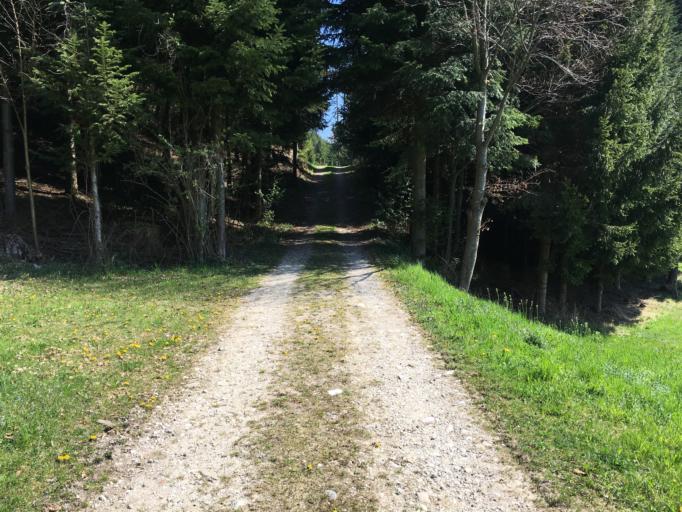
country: AT
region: Upper Austria
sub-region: Politischer Bezirk Vocklabruck
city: Vocklamarkt
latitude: 48.0028
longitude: 13.4702
